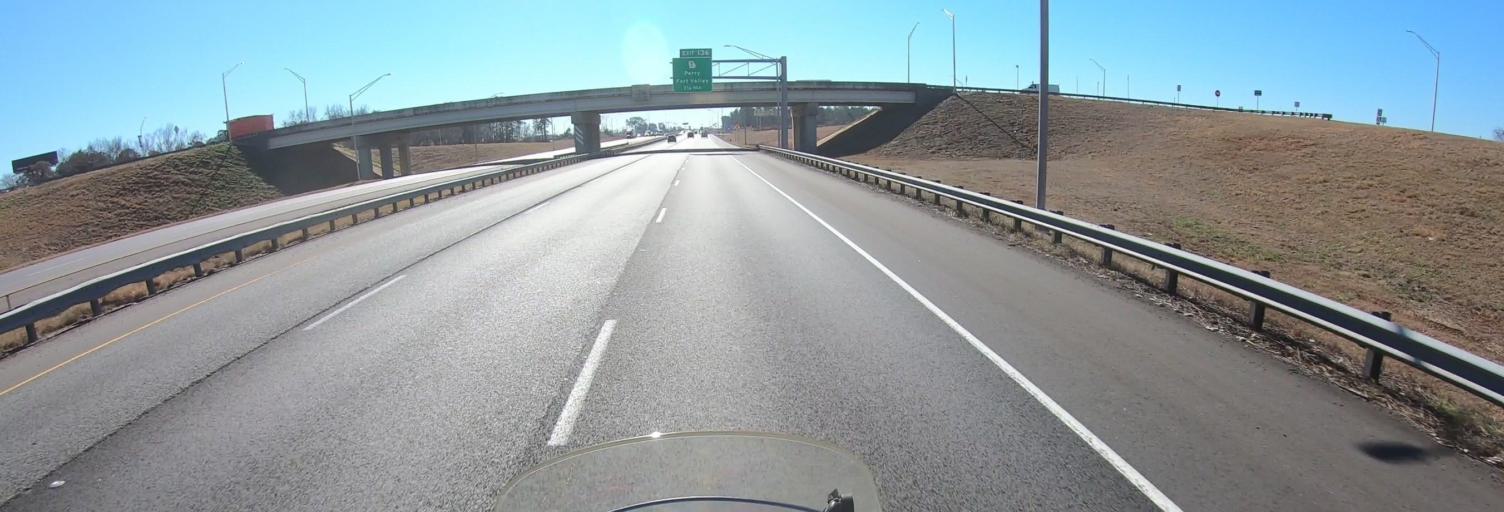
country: US
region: Georgia
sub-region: Houston County
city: Perry
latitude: 32.4953
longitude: -83.7437
